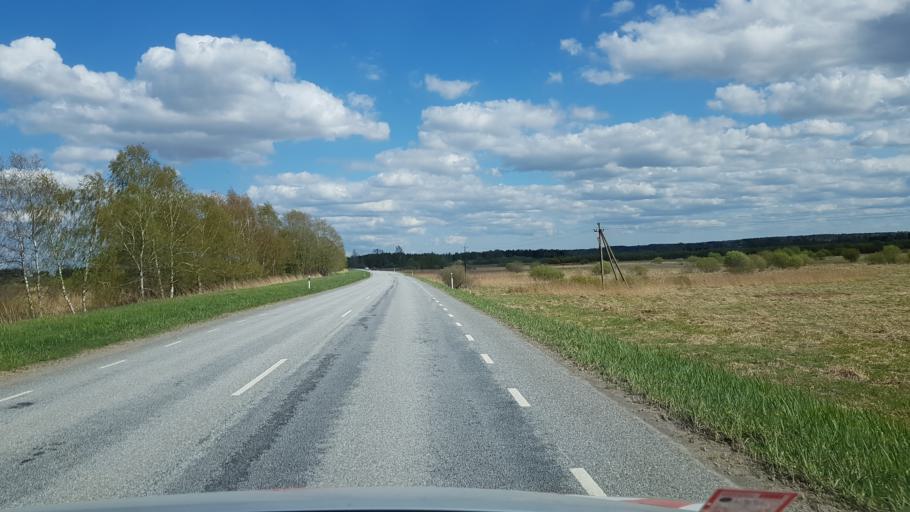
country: EE
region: Tartu
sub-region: UElenurme vald
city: Ulenurme
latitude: 58.3283
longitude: 26.7466
